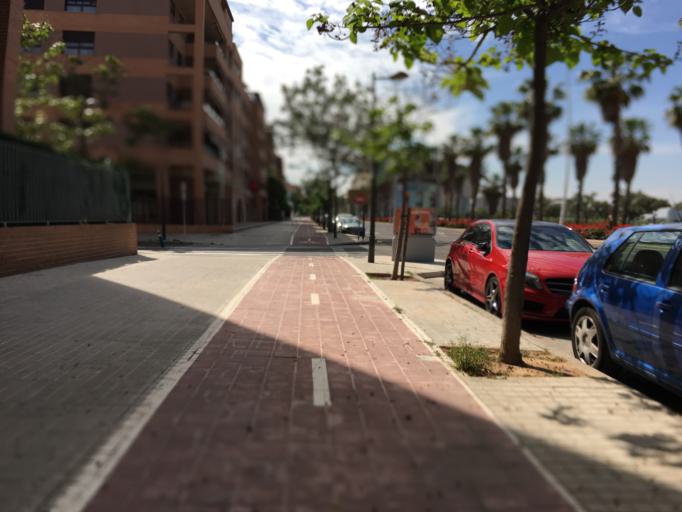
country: ES
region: Valencia
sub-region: Provincia de Valencia
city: Mislata
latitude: 39.4905
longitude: -0.4067
